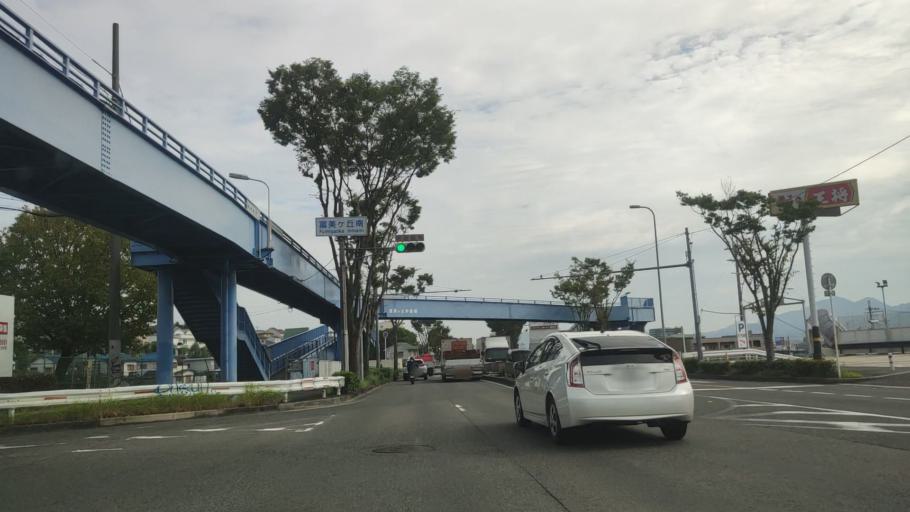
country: JP
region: Osaka
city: Tondabayashicho
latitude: 34.5008
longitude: 135.5904
